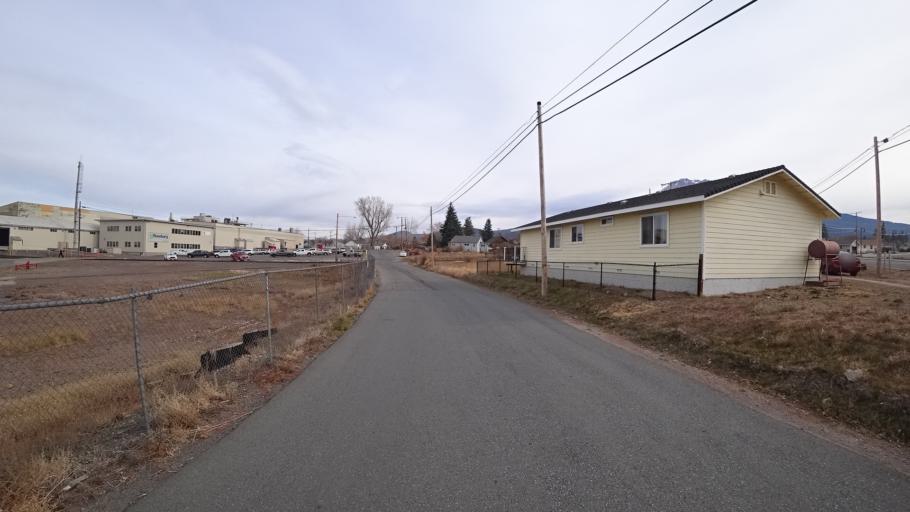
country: US
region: California
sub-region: Siskiyou County
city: Weed
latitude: 41.4314
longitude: -122.3800
